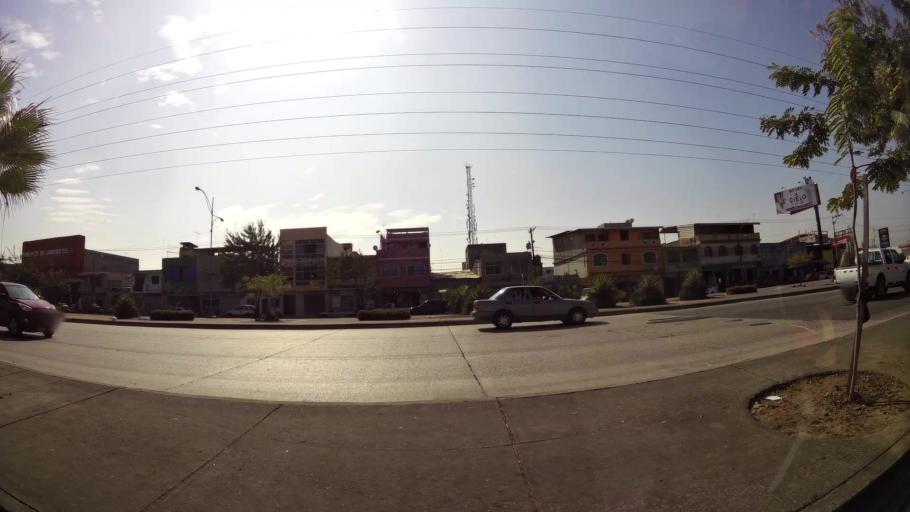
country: EC
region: Guayas
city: Eloy Alfaro
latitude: -2.0908
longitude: -79.9132
